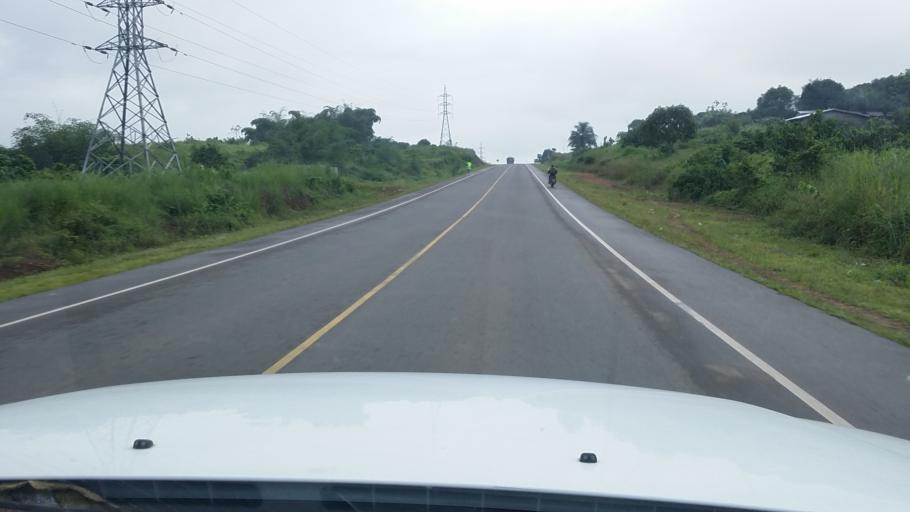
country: LR
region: Montserrado
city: Bensonville City
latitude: 6.3908
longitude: -10.5867
